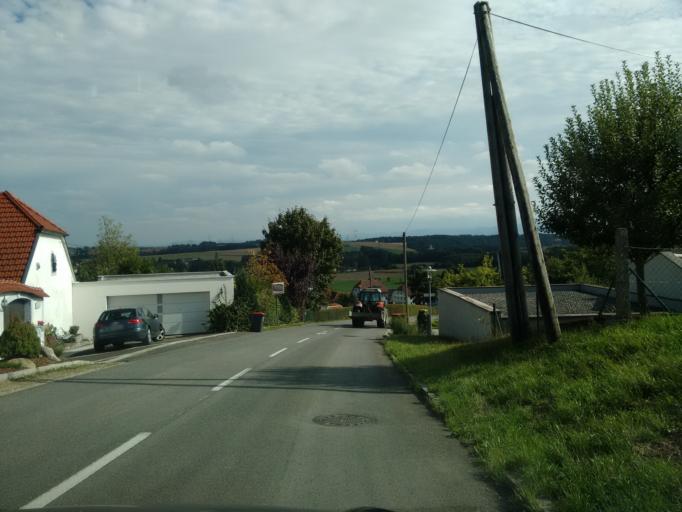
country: AT
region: Upper Austria
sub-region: Politischer Bezirk Steyr-Land
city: Bad Hall
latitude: 48.1083
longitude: 14.1876
